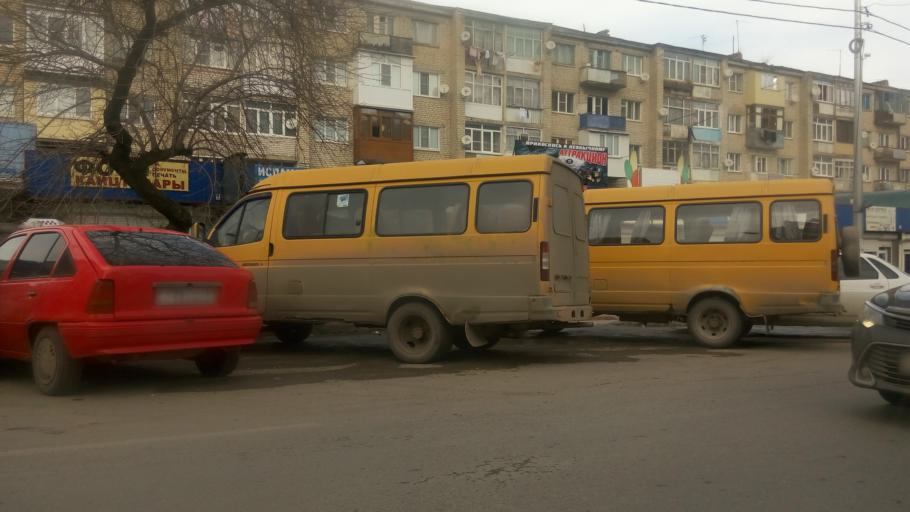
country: RU
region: Karachayevo-Cherkesiya
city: Karachayevsk
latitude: 43.7707
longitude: 41.9094
